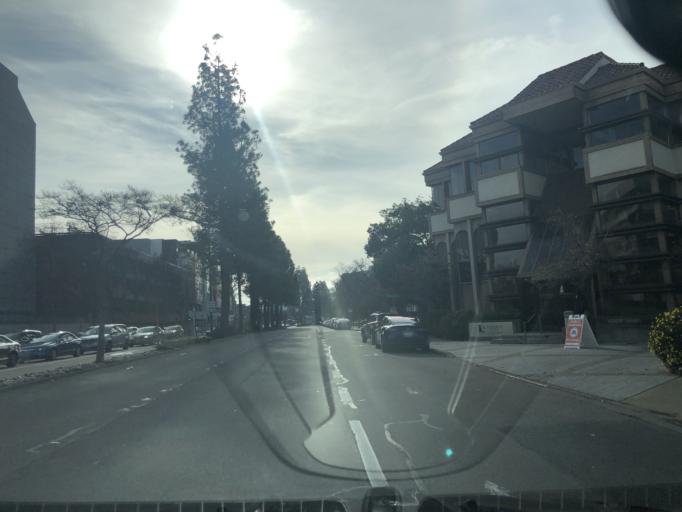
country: US
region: California
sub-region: Contra Costa County
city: Walnut Creek
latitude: 37.9012
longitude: -122.0644
